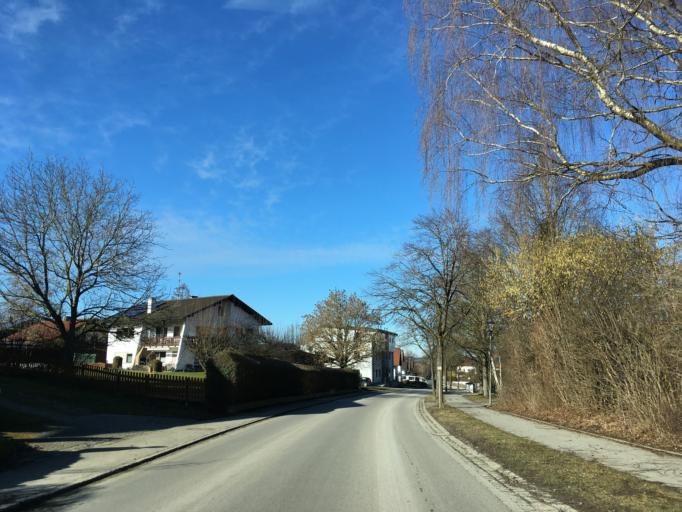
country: DE
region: Bavaria
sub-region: Upper Bavaria
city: Obertaufkirchen
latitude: 48.2615
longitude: 12.2795
